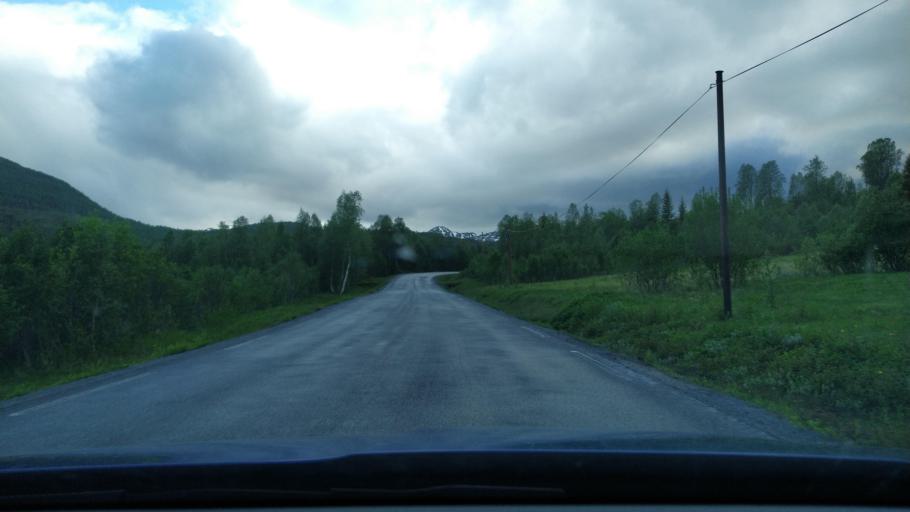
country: NO
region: Troms
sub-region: Dyroy
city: Brostadbotn
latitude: 69.0547
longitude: 17.8085
